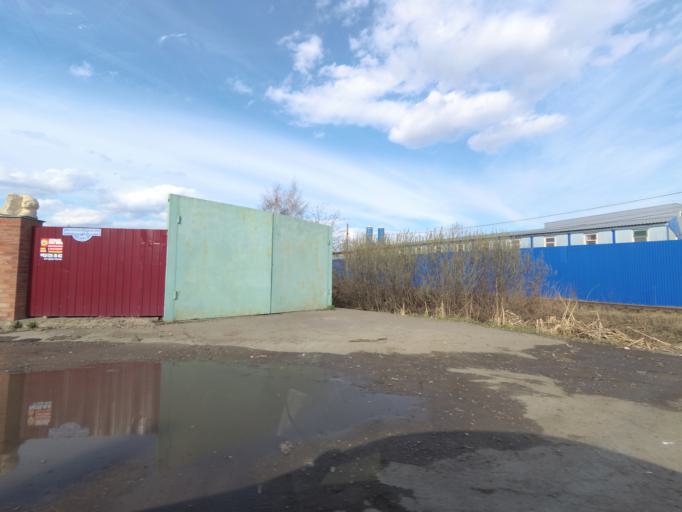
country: RU
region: Moskovskaya
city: Lobnya
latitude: 56.0111
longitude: 37.4374
